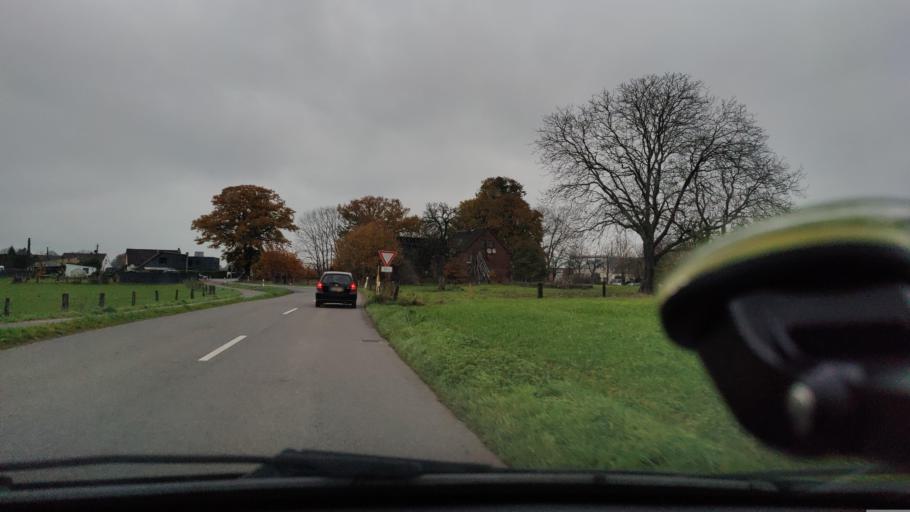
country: DE
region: North Rhine-Westphalia
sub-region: Regierungsbezirk Dusseldorf
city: Kamp-Lintfort
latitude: 51.5453
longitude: 6.5442
